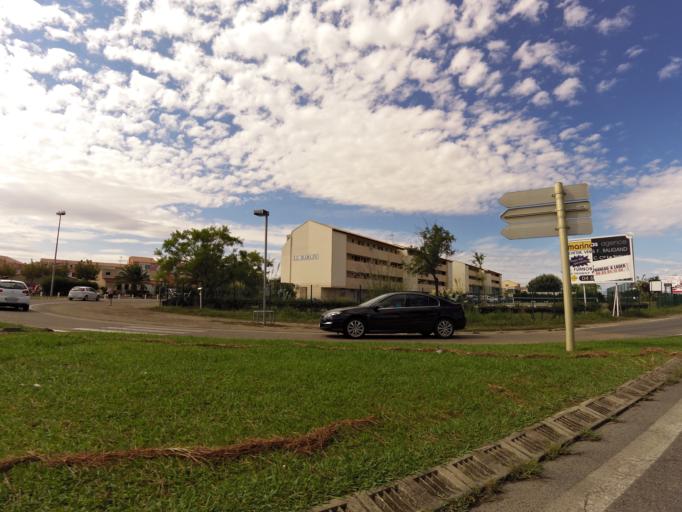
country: FR
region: Languedoc-Roussillon
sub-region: Departement du Gard
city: Le Grau-du-Roi
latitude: 43.5269
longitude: 4.1501
